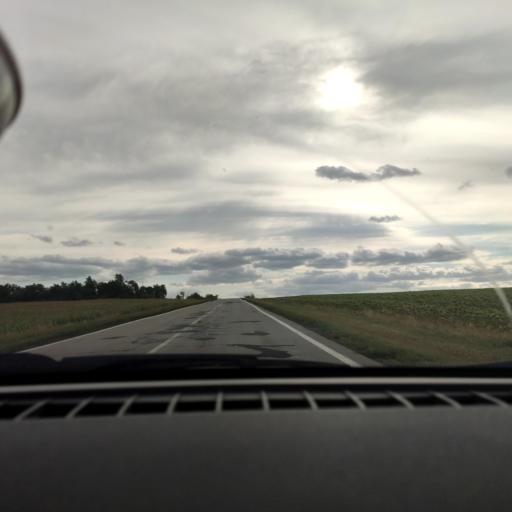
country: RU
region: Samara
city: Krasnyy Yar
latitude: 53.4344
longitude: 50.5637
